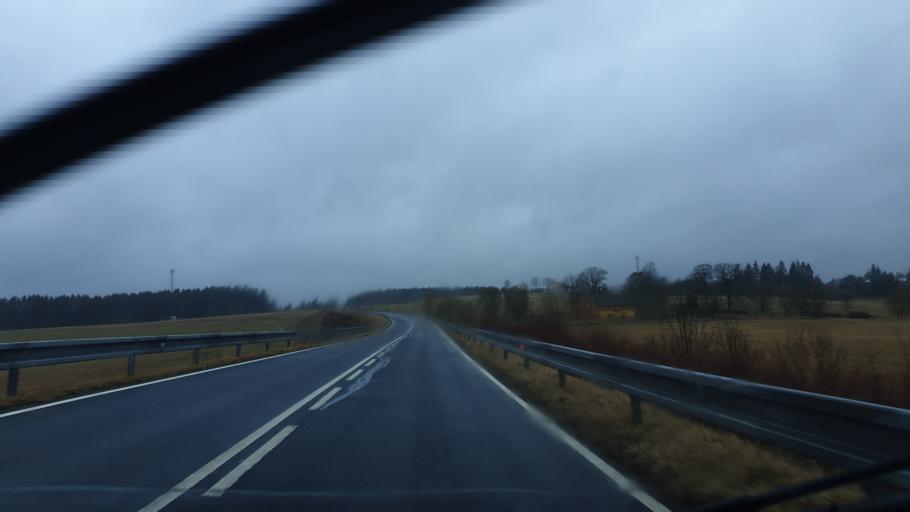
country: CZ
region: Karlovarsky
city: Hranice
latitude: 50.2967
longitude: 12.1686
